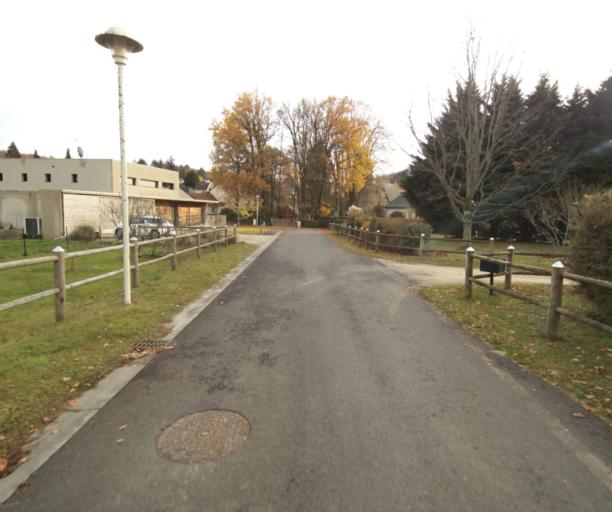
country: FR
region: Limousin
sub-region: Departement de la Correze
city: Sainte-Fortunade
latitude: 45.2043
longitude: 1.7700
